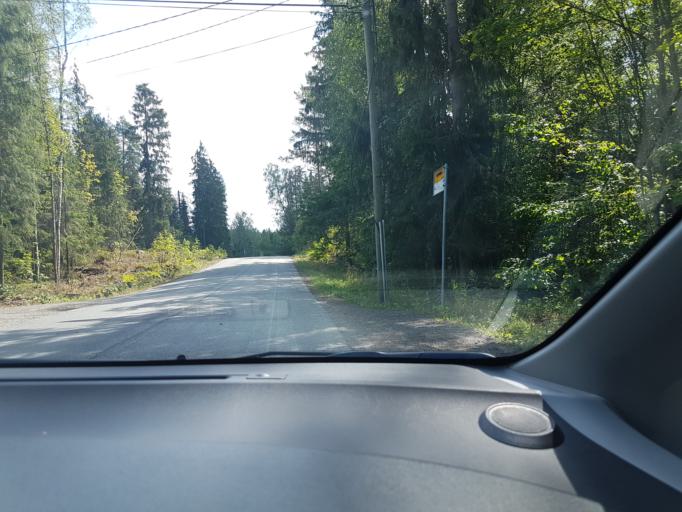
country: FI
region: Uusimaa
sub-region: Helsinki
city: Kilo
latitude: 60.3287
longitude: 24.7631
